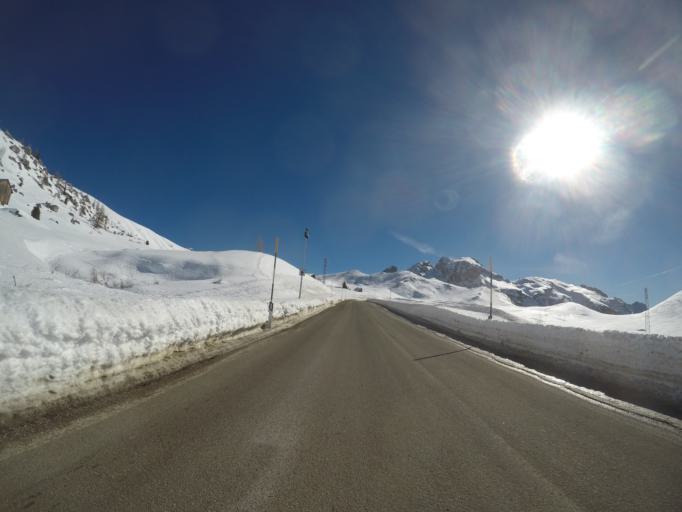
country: IT
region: Veneto
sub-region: Provincia di Belluno
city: Selva di Cadore
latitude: 46.4859
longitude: 12.0441
